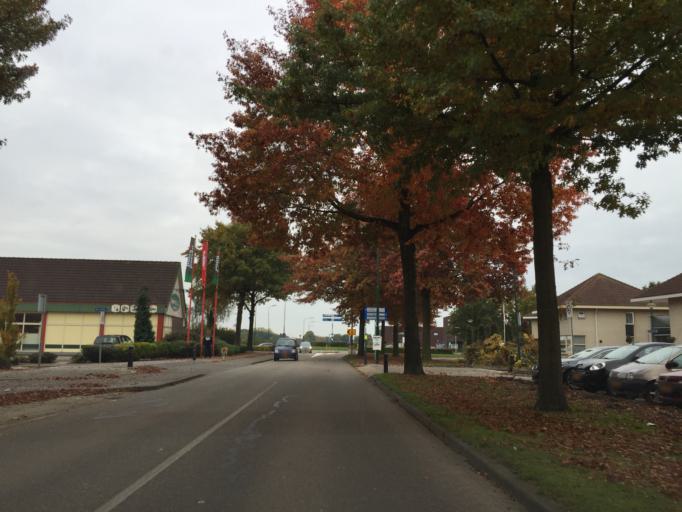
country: NL
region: North Brabant
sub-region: Gemeente Waalwijk
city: Waalwijk
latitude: 51.6523
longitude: 5.0325
